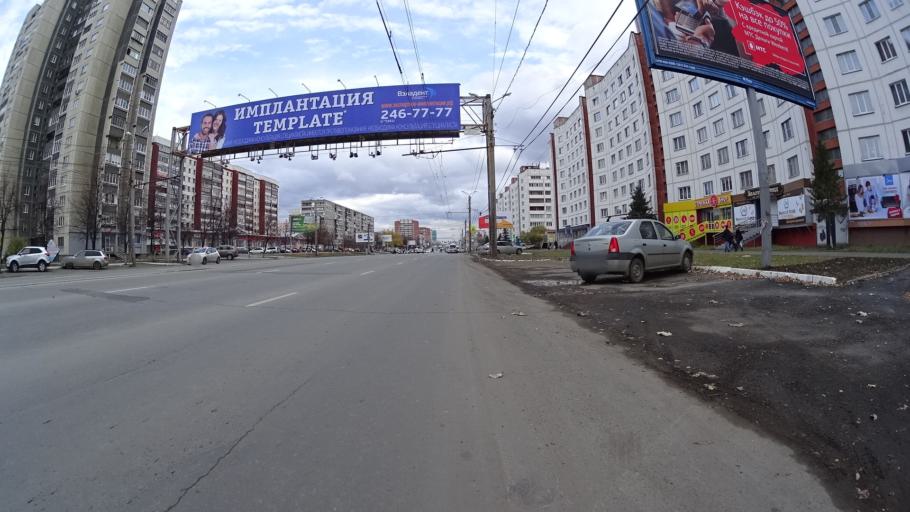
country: RU
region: Chelyabinsk
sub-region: Gorod Chelyabinsk
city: Chelyabinsk
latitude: 55.1943
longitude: 61.3121
